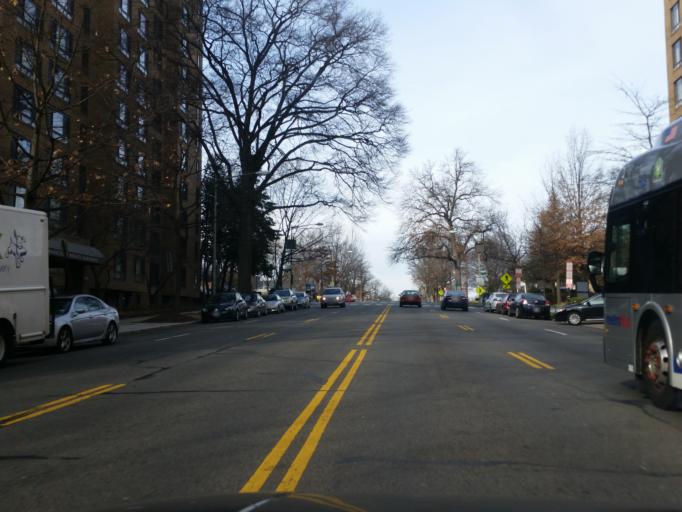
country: US
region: Maryland
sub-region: Montgomery County
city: Chevy Chase Village
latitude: 38.9527
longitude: -77.0685
